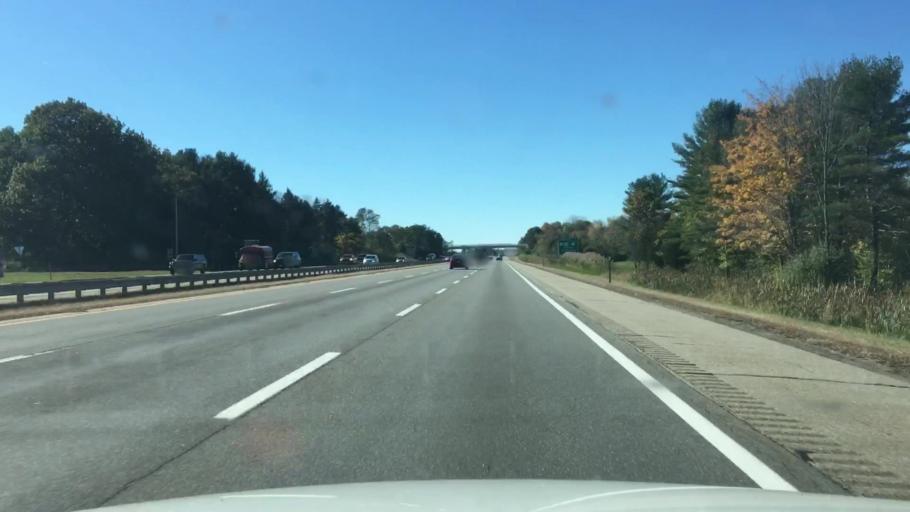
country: US
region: Maine
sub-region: York County
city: Kittery
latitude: 43.1284
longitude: -70.7193
